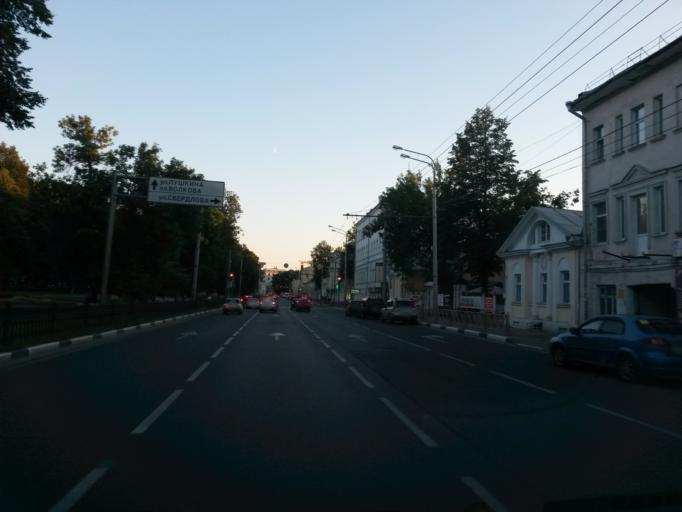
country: RU
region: Jaroslavl
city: Yaroslavl
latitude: 57.6298
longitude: 39.8859
